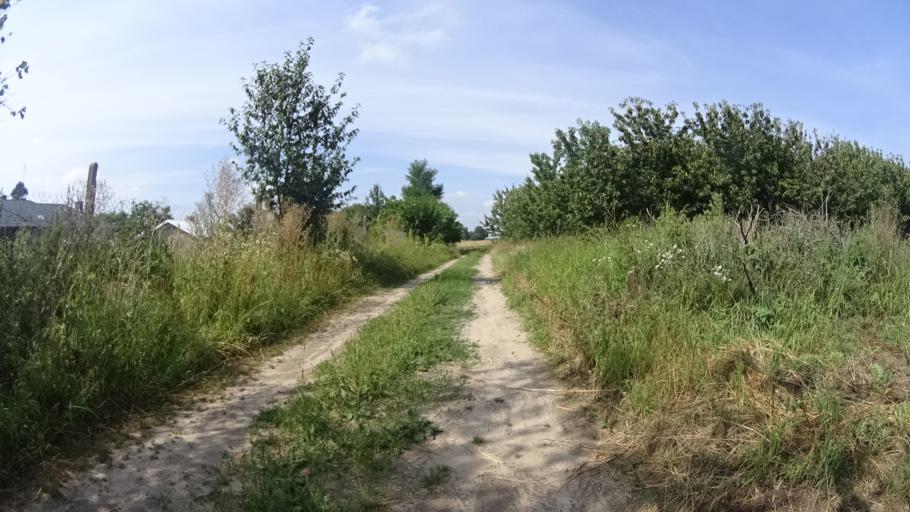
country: PL
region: Masovian Voivodeship
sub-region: Powiat grojecki
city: Goszczyn
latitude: 51.6860
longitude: 20.8413
